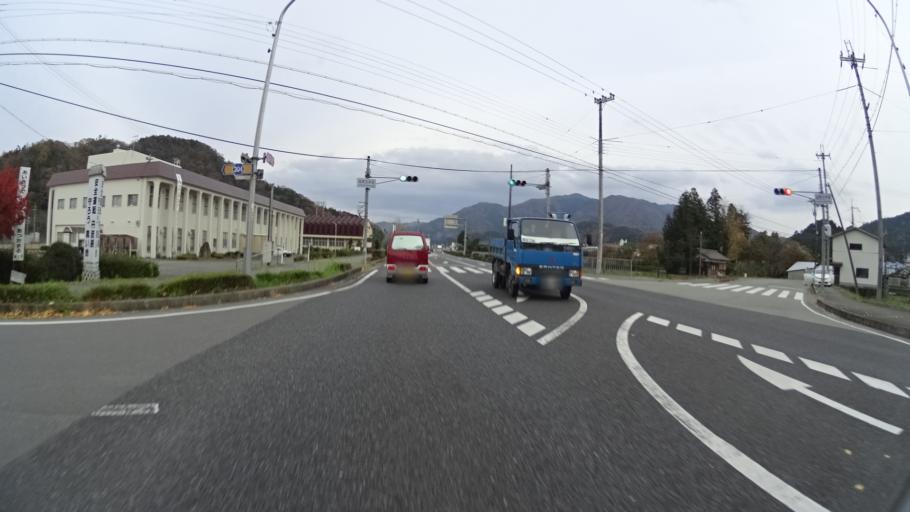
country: JP
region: Hyogo
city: Sasayama
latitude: 35.0701
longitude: 135.2785
